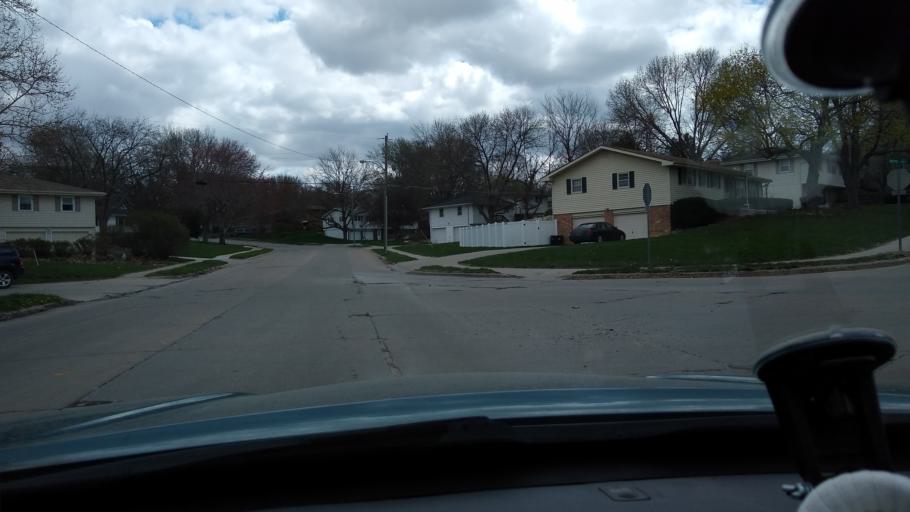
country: US
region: Nebraska
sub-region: Douglas County
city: Ralston
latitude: 41.2277
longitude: -96.0943
